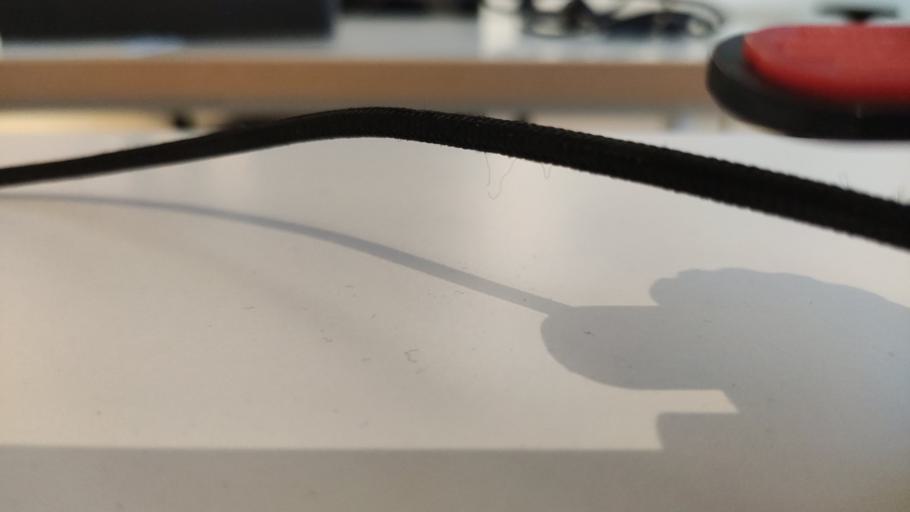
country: RU
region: Moskovskaya
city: Sychevo
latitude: 55.8409
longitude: 36.3353
